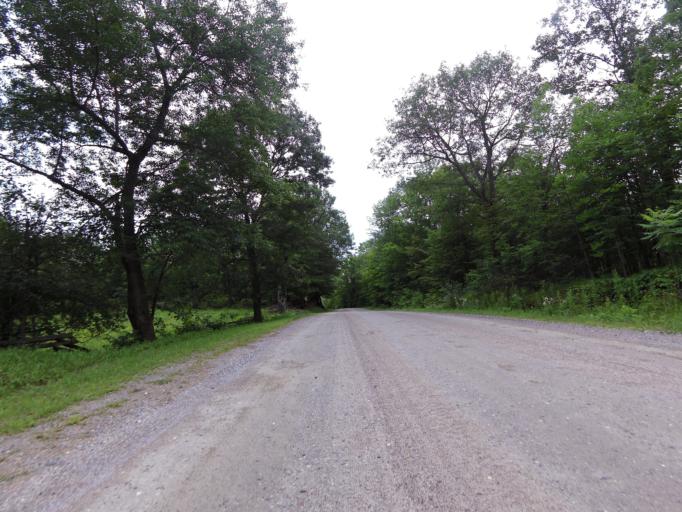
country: CA
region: Ontario
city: Perth
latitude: 44.7926
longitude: -76.6396
